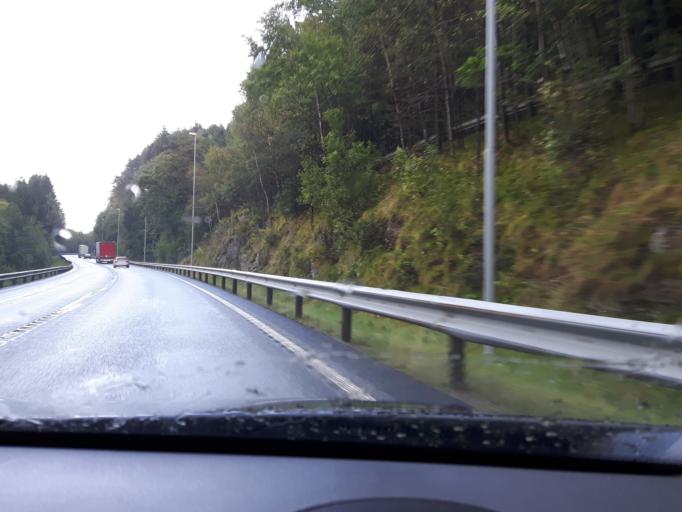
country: NO
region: Vest-Agder
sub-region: Sogne
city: Sogne
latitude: 58.0939
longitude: 7.7494
